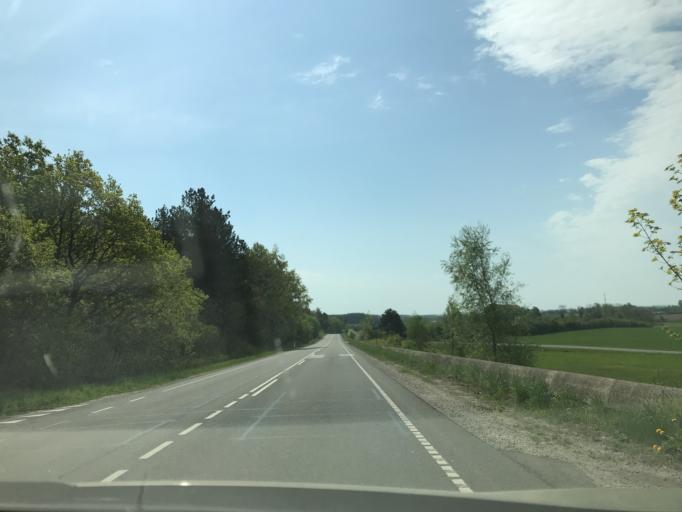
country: DK
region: South Denmark
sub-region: Middelfart Kommune
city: Ejby
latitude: 55.3902
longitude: 9.9140
